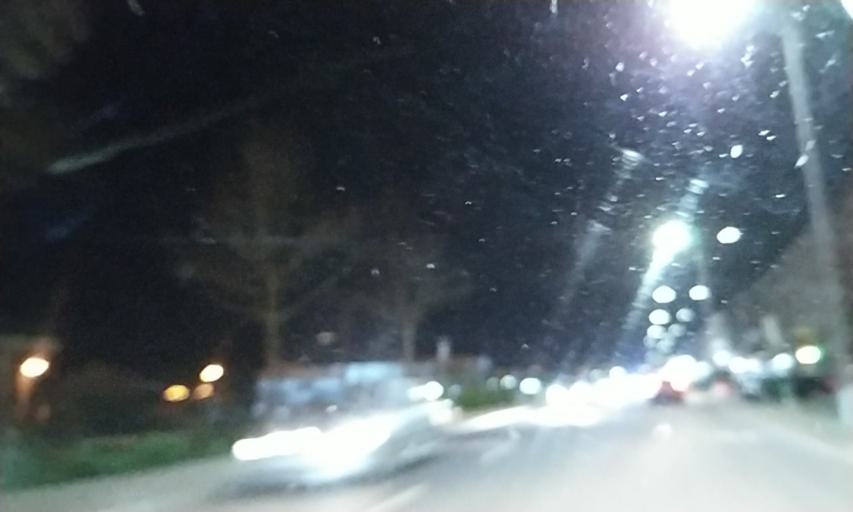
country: PT
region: Castelo Branco
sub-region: Concelho do Fundao
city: Fundao
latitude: 40.1499
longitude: -7.4986
